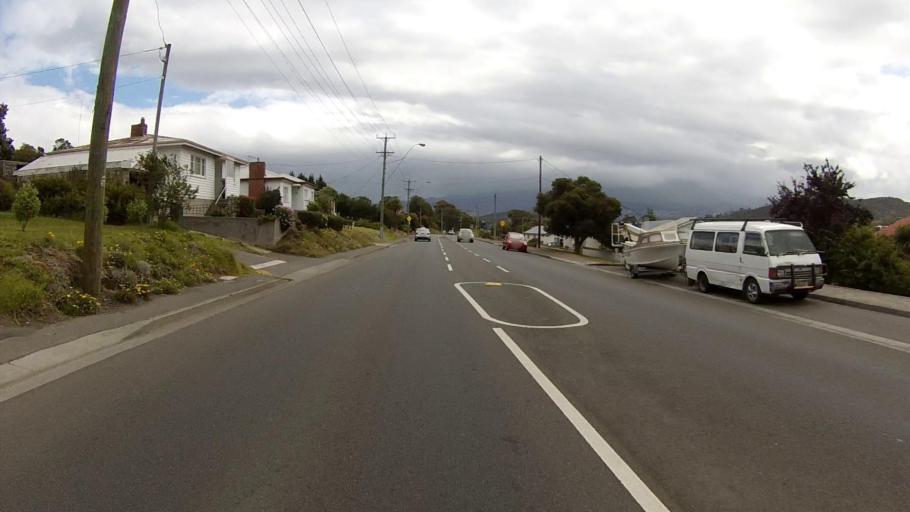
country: AU
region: Tasmania
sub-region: Clarence
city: Warrane
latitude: -42.8587
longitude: 147.3847
